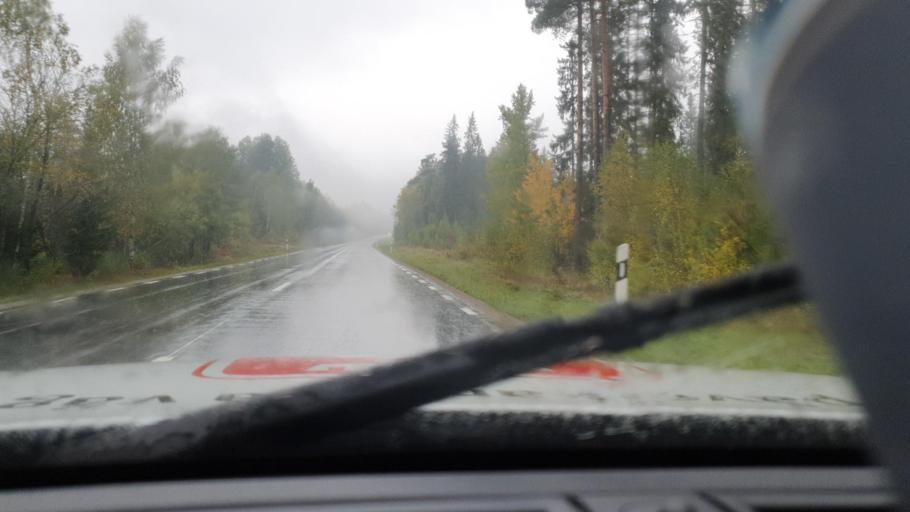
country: SE
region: Uppsala
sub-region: Tierps Kommun
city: Tierp
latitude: 60.2778
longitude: 17.5965
